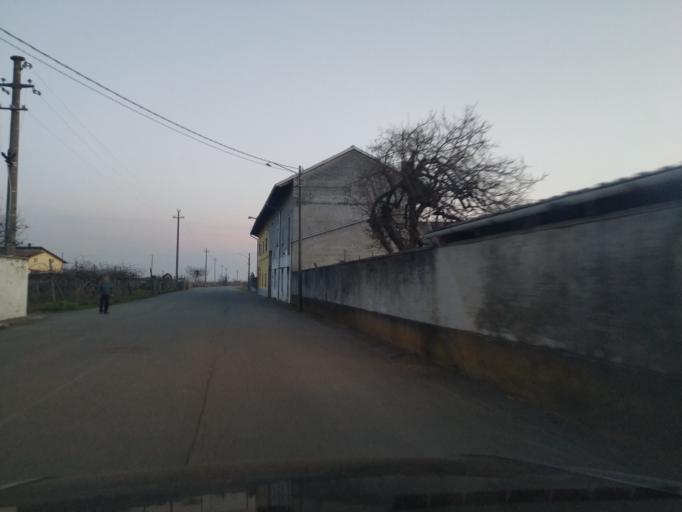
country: IT
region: Piedmont
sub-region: Provincia di Vercelli
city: Borgo d'Ale
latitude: 45.3444
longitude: 8.0522
